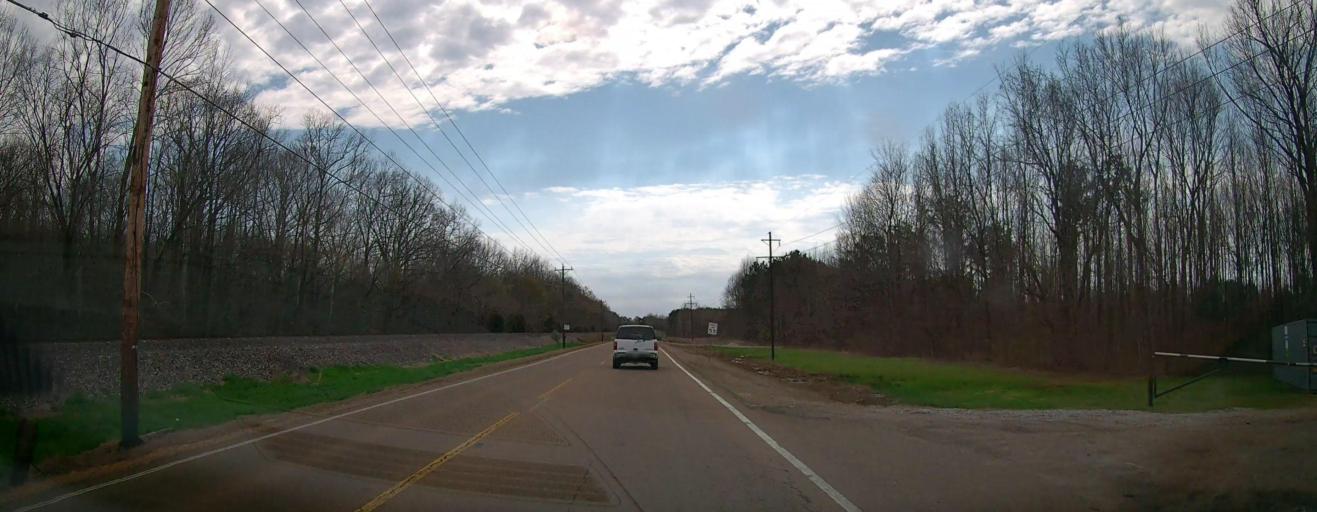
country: US
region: Mississippi
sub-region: Marshall County
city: Byhalia
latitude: 34.8974
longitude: -89.7399
